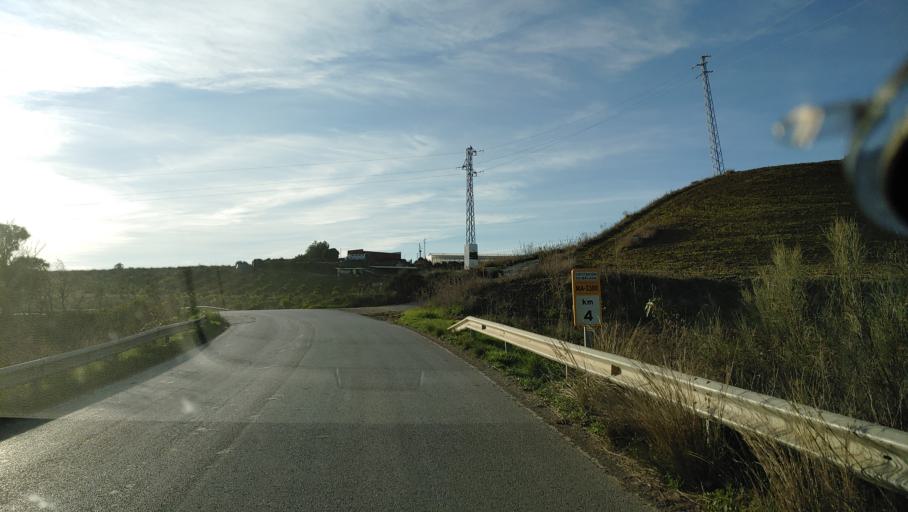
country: ES
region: Andalusia
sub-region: Provincia de Malaga
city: Cartama
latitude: 36.6823
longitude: -4.6163
